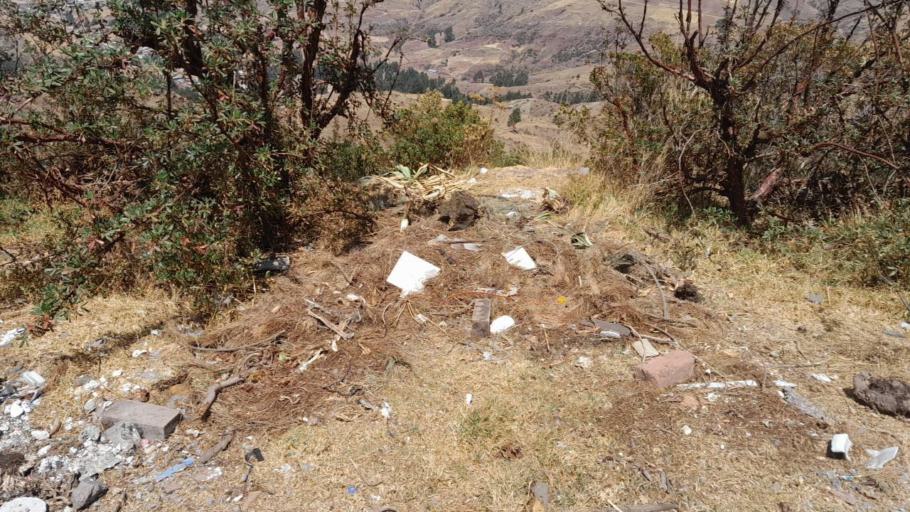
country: PE
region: Cusco
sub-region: Provincia de Cusco
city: Cusco
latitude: -13.4907
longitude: -71.9324
